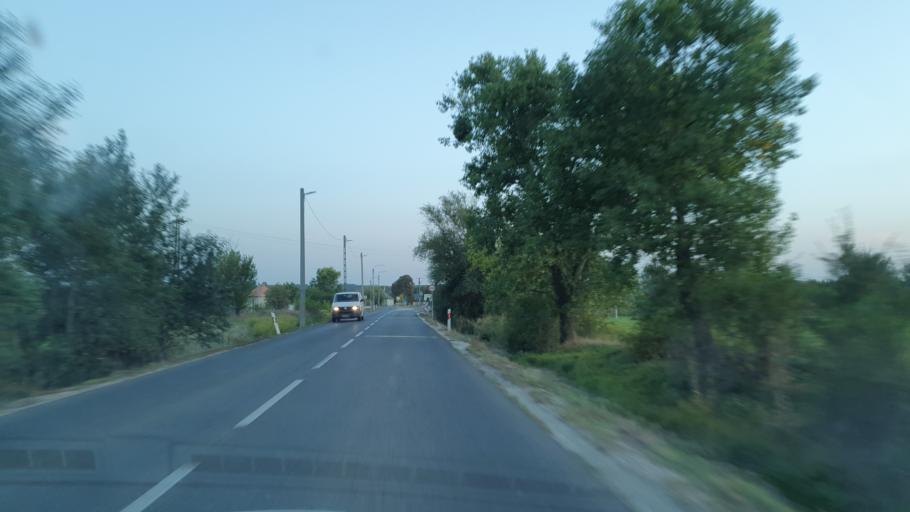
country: HU
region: Fejer
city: Zamoly
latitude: 47.3274
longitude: 18.4078
